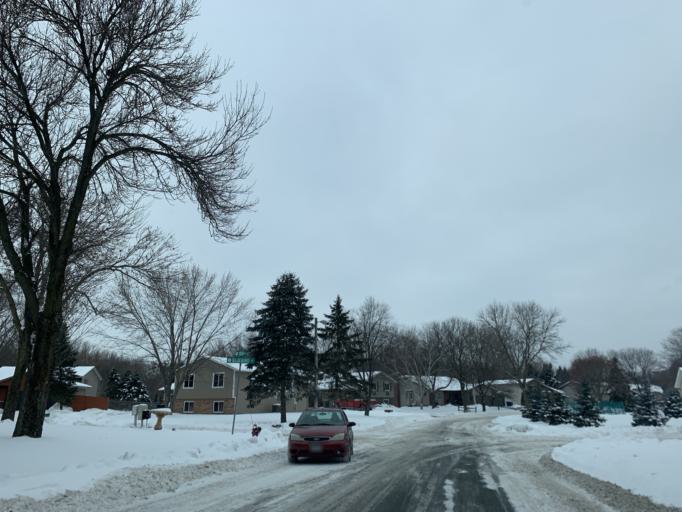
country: US
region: Minnesota
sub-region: Anoka County
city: Coon Rapids
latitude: 45.1636
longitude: -93.3013
